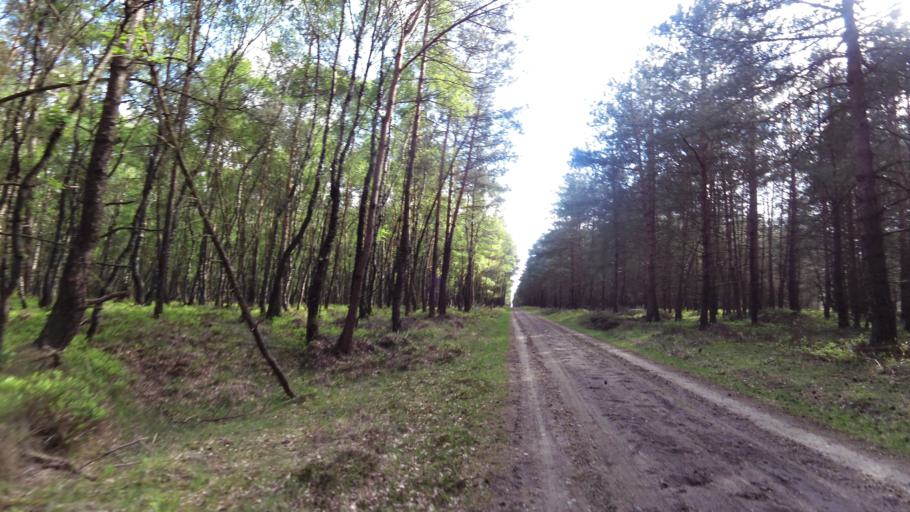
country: NL
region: Gelderland
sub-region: Gemeente Rozendaal
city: Rozendaal
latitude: 52.0711
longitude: 5.9536
